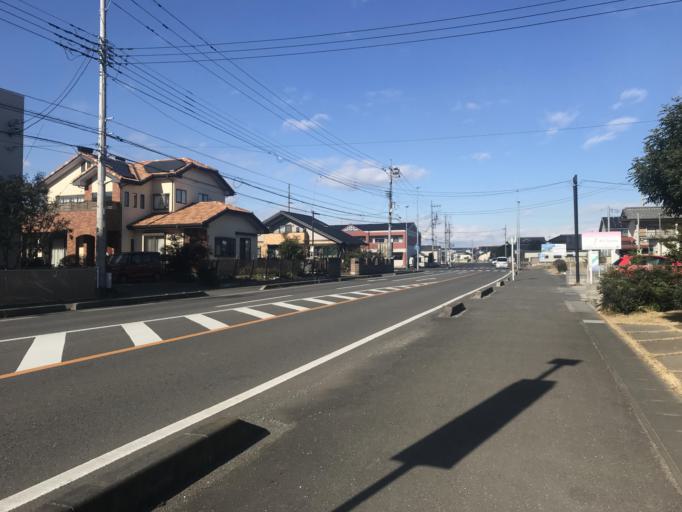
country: JP
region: Tochigi
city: Kaminokawa
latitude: 36.3814
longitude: 139.8758
